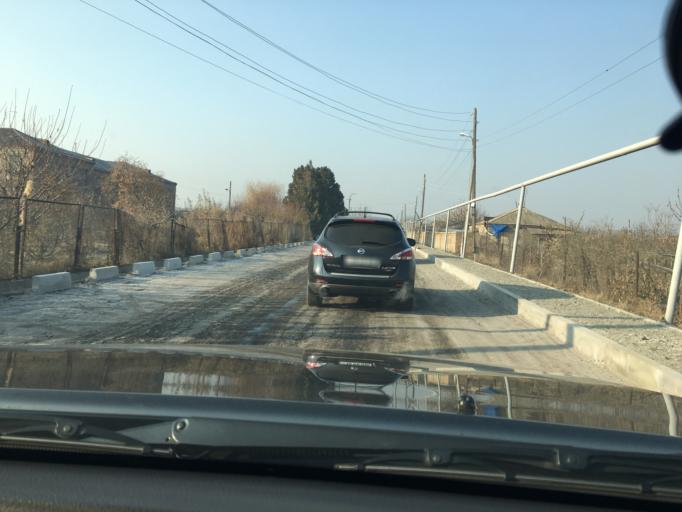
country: AM
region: Armavir
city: Janfida
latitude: 40.0429
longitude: 44.0246
